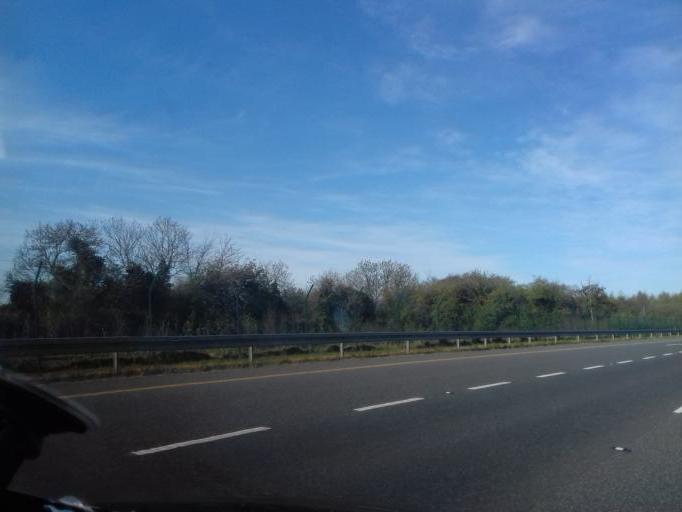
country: IE
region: Leinster
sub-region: An Mhi
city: Navan
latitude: 53.6176
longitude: -6.6891
